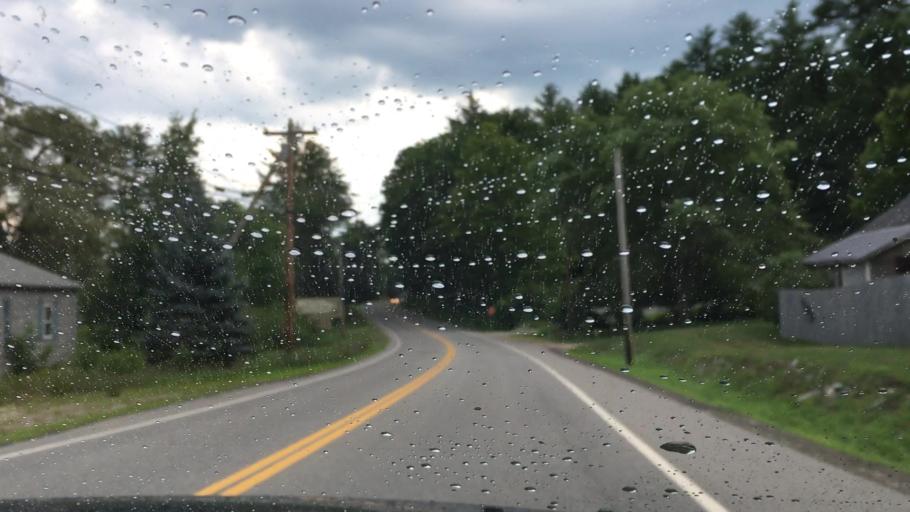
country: US
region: New Hampshire
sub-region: Belknap County
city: Meredith
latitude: 43.6779
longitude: -71.5080
